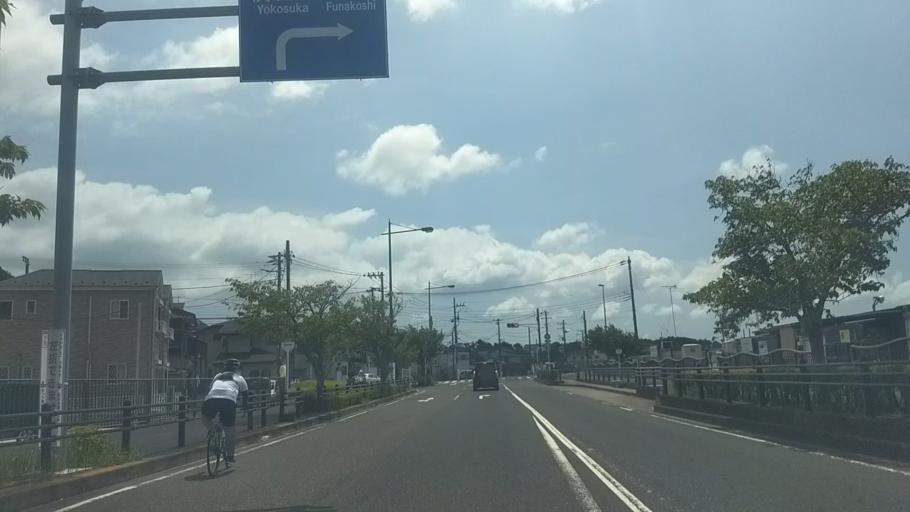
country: JP
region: Kanagawa
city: Yokosuka
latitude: 35.3270
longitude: 139.6313
